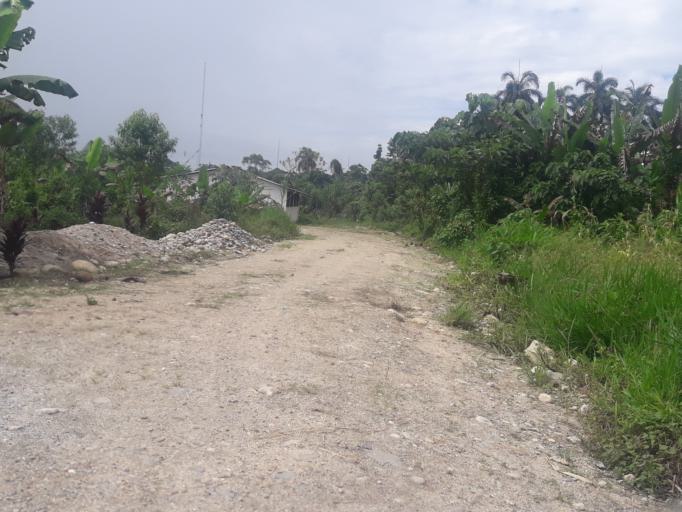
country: EC
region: Napo
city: Tena
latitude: -0.9746
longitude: -77.8486
